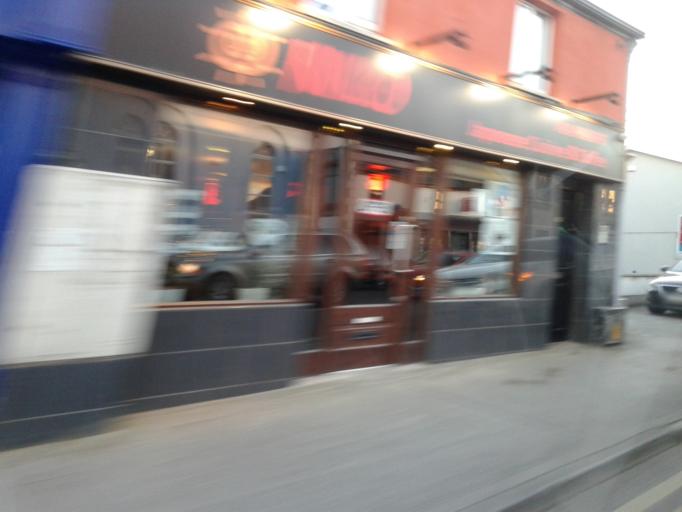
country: IE
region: Leinster
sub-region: Lu
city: Drogheda
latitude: 53.7164
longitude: -6.3581
